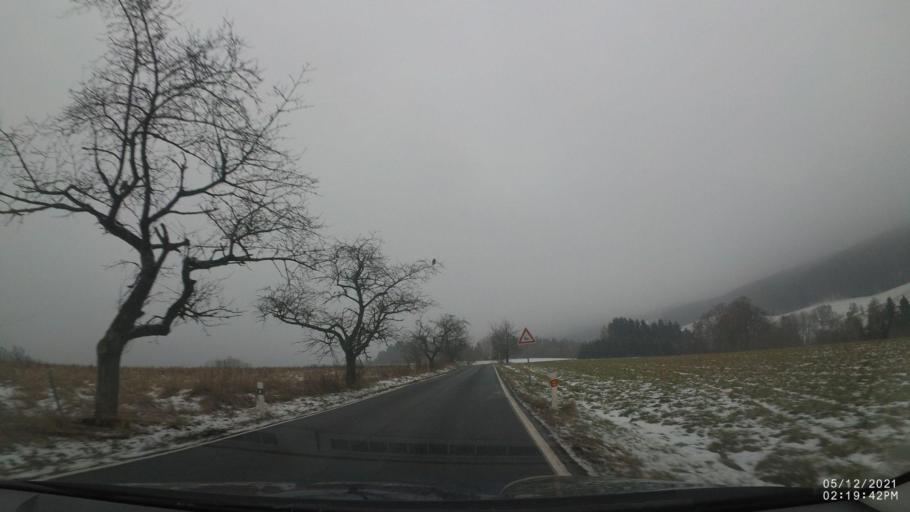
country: CZ
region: Kralovehradecky
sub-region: Okres Nachod
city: Nachod
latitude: 50.4453
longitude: 16.1413
